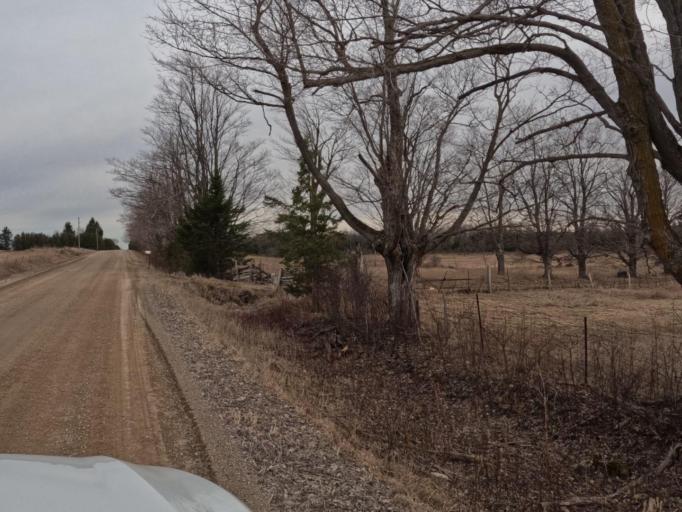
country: CA
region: Ontario
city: Shelburne
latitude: 43.9349
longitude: -80.2587
